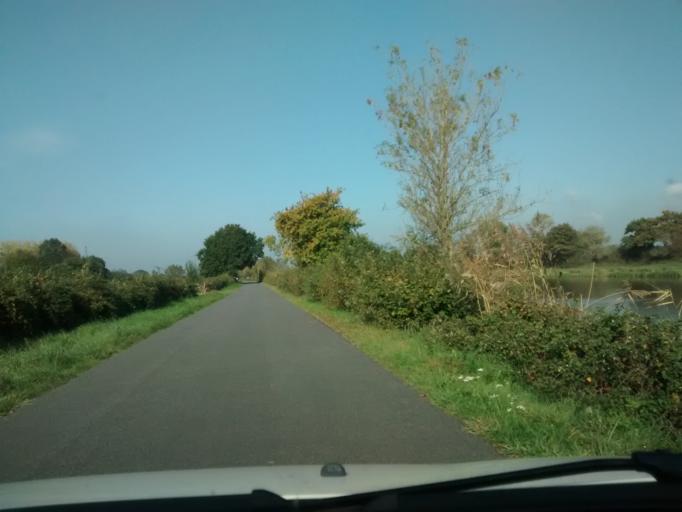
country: FR
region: Pays de la Loire
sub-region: Departement de la Loire-Atlantique
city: Vue
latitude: 47.2430
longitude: -1.8820
